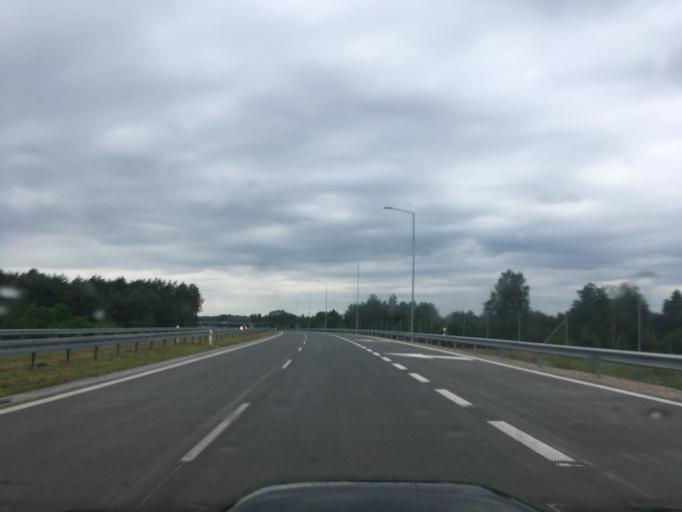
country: PL
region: Masovian Voivodeship
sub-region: Powiat piaseczynski
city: Gora Kalwaria
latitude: 51.9755
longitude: 21.1893
